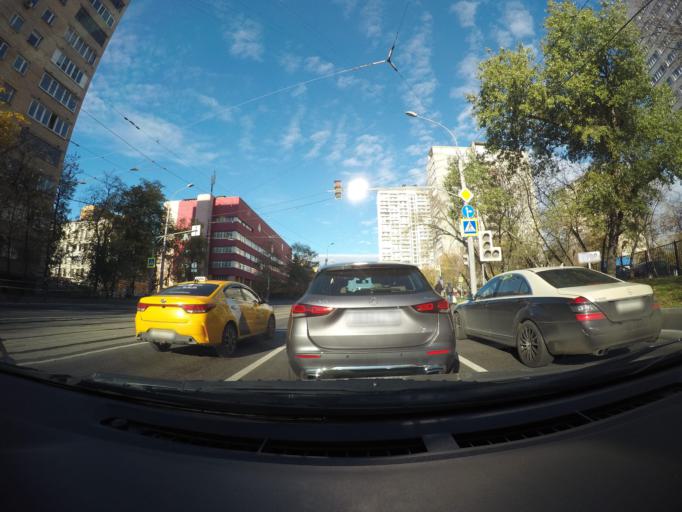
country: RU
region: Moscow
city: Rostokino
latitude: 55.8251
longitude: 37.6524
